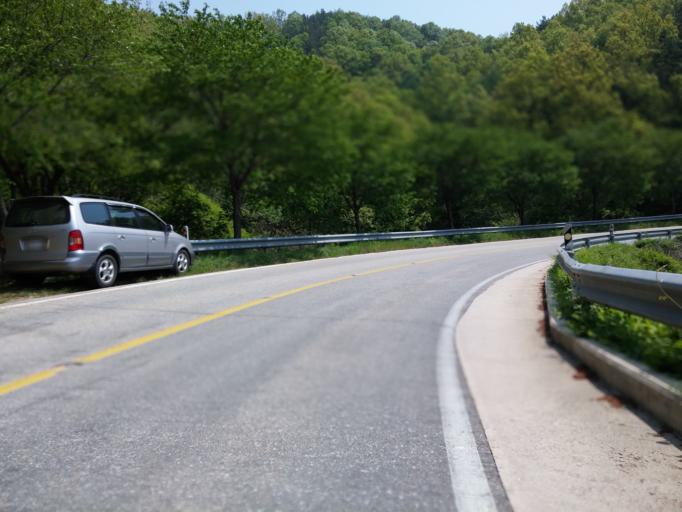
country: KR
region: Daejeon
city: Sintansin
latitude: 36.4347
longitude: 127.5627
